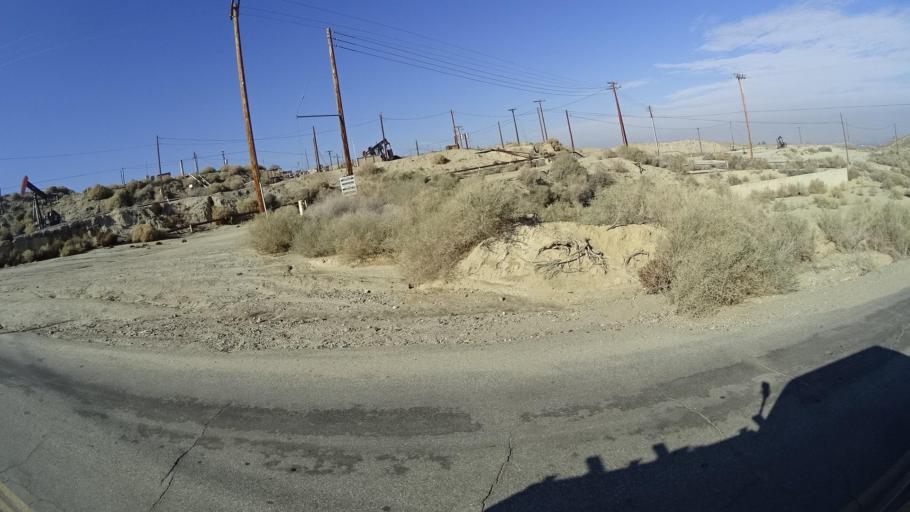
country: US
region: California
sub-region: Kern County
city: Taft Heights
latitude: 35.1211
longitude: -119.4736
